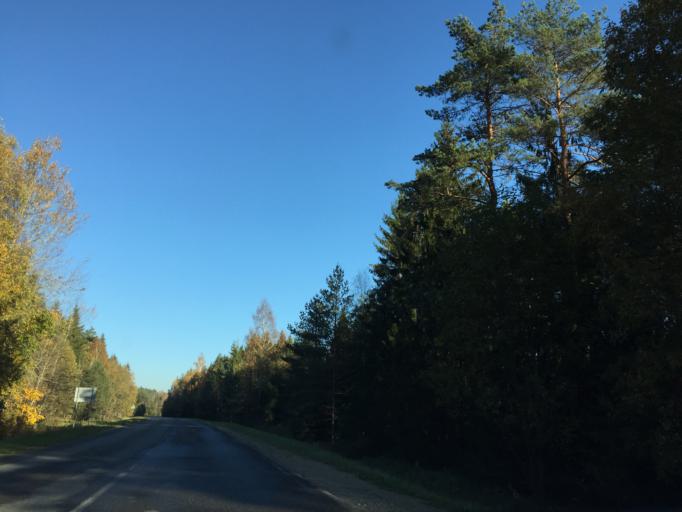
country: LT
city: Plateliai
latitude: 56.0619
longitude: 21.8781
